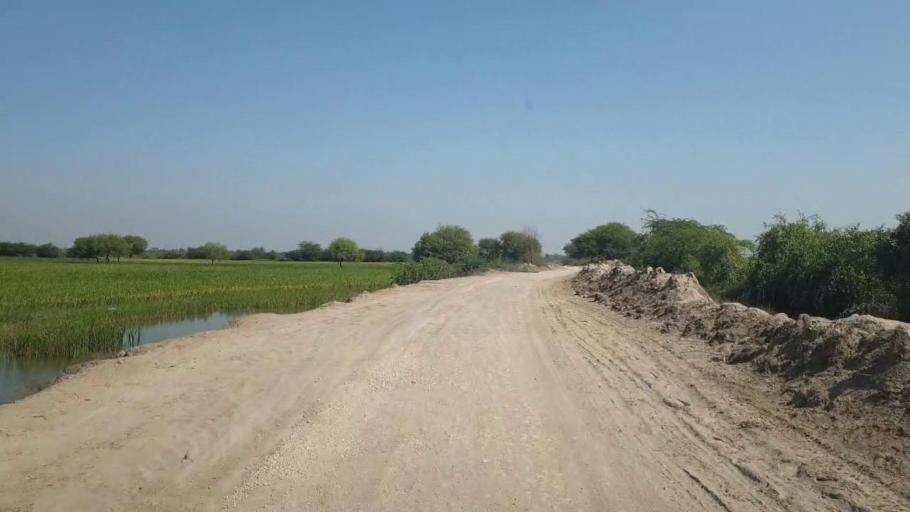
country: PK
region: Sindh
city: Talhar
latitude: 24.7938
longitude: 68.8063
